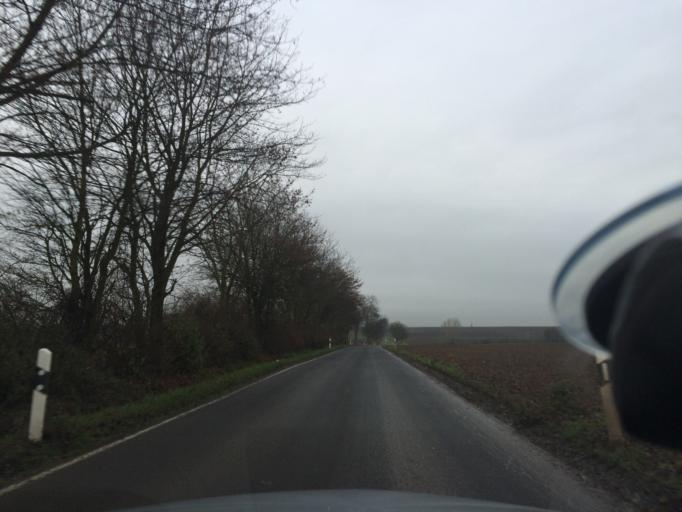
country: DE
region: Rheinland-Pfalz
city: Biebelnheim
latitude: 49.8072
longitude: 8.1786
